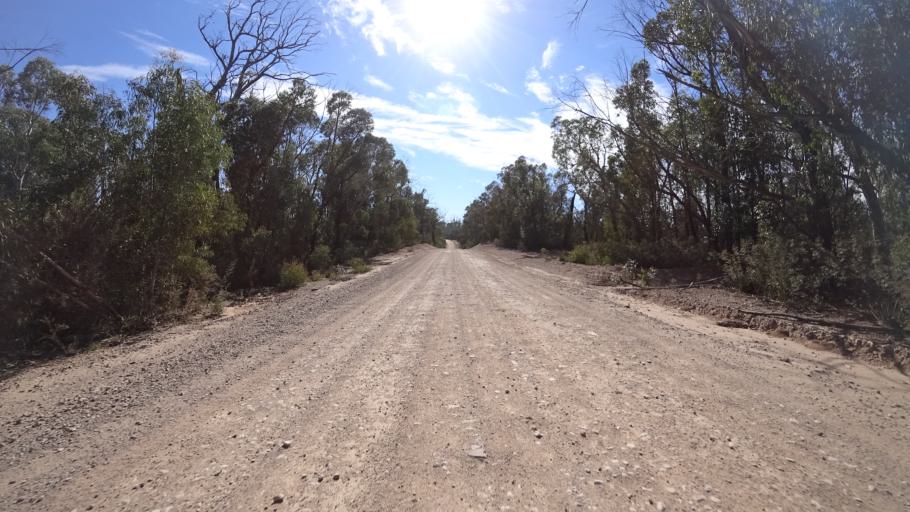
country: AU
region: New South Wales
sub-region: Lithgow
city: Lithgow
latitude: -33.4327
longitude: 150.1902
